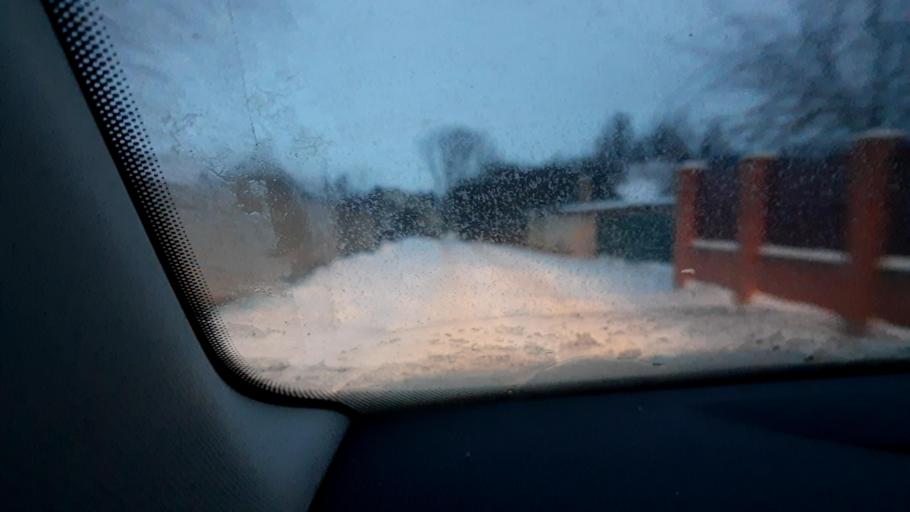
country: RU
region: Moskovskaya
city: Yam
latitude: 55.4841
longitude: 37.7185
